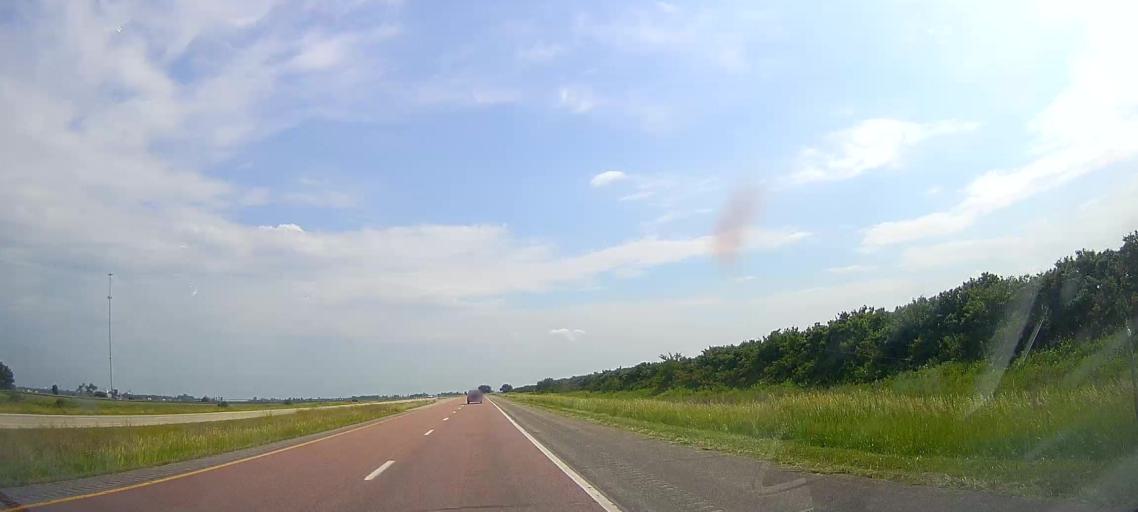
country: US
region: Iowa
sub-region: Monona County
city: Onawa
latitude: 41.9579
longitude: -96.1032
